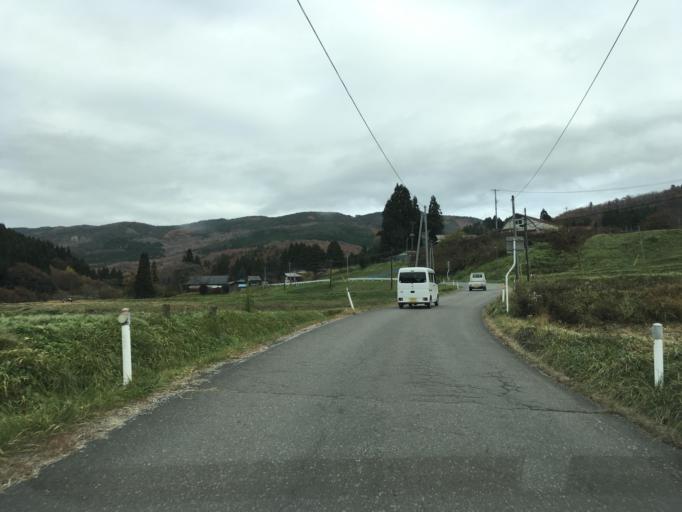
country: JP
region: Iwate
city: Mizusawa
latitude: 39.1083
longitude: 141.3278
